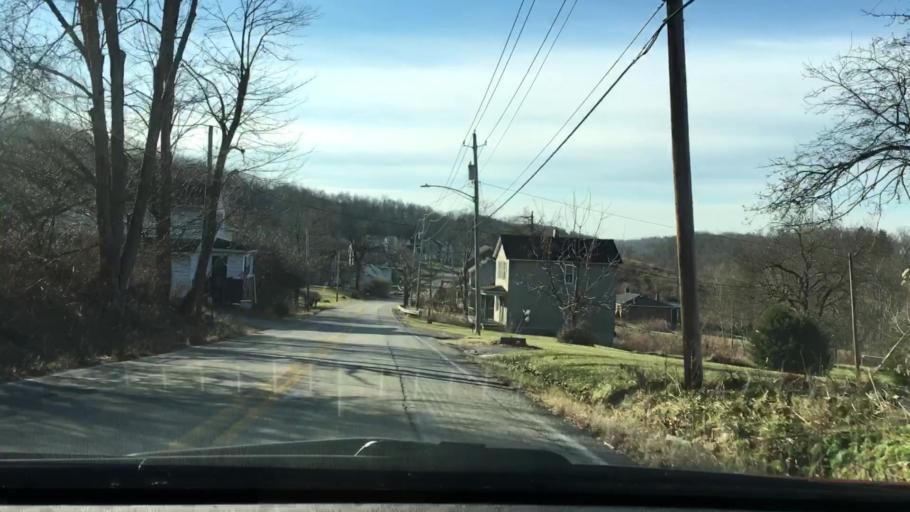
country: US
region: Pennsylvania
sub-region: Westmoreland County
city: Irwin
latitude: 40.2848
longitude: -79.6920
